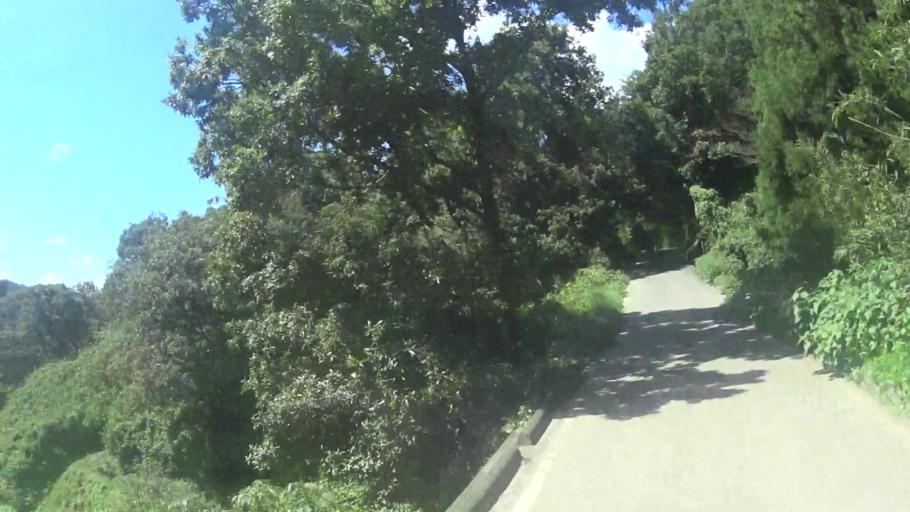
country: JP
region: Nara
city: Nara-shi
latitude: 34.7184
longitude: 135.8862
